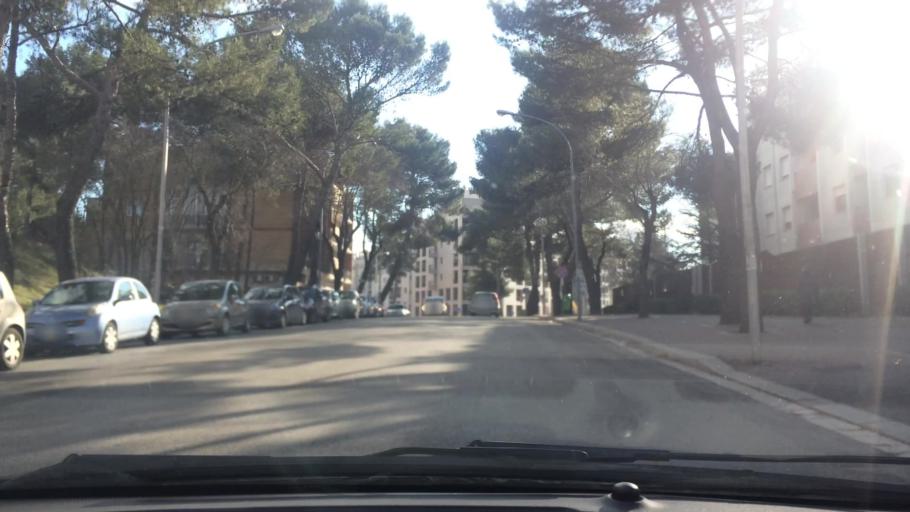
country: IT
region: Basilicate
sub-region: Provincia di Matera
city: Matera
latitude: 40.6698
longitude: 16.5982
